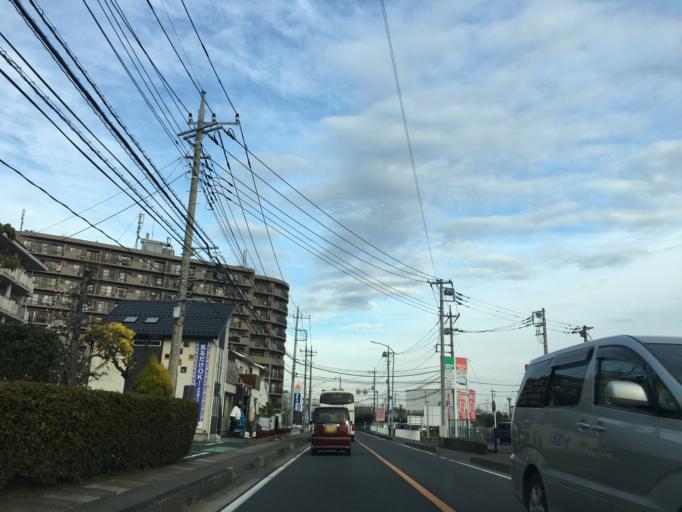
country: JP
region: Saitama
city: Kawagoe
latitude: 35.9176
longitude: 139.4417
